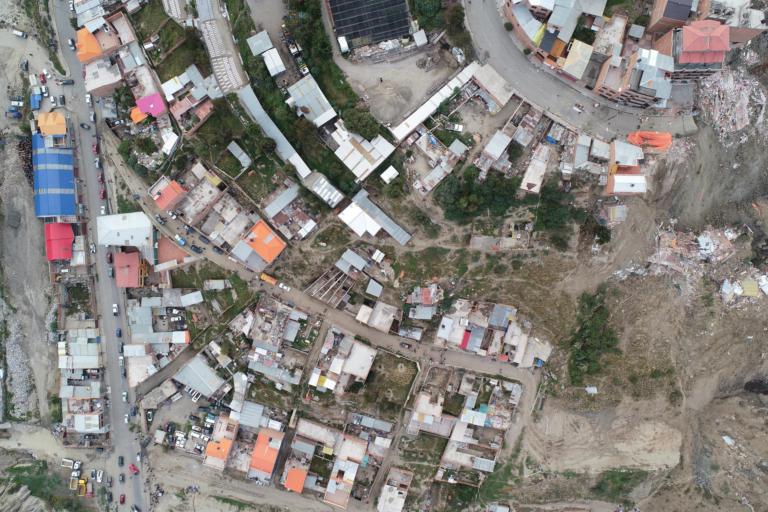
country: BO
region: La Paz
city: La Paz
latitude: -16.5205
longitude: -68.1233
